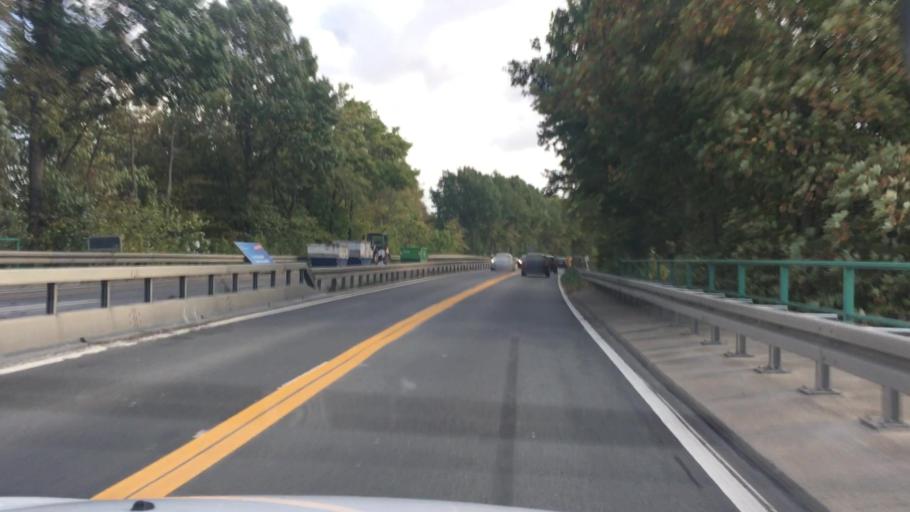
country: DE
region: Lower Saxony
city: Neustadt am Rubenberge
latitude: 52.5109
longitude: 9.4681
